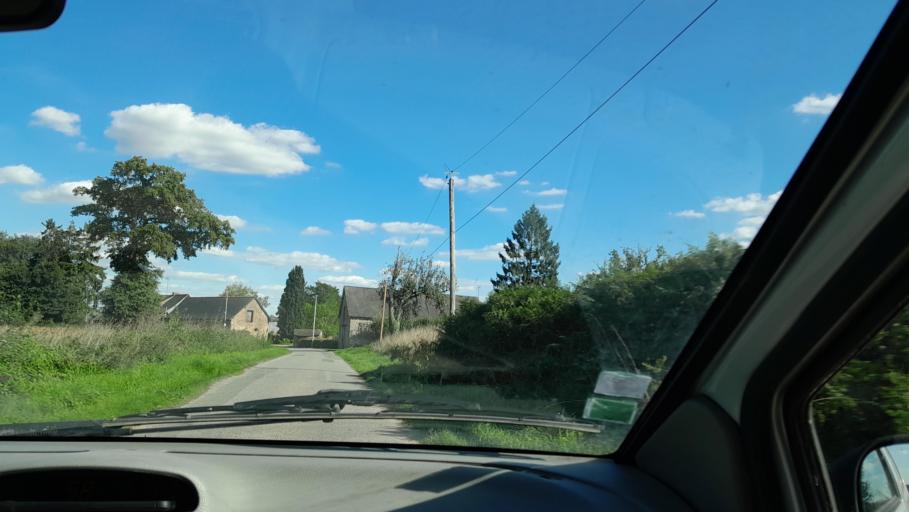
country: FR
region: Pays de la Loire
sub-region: Departement de la Mayenne
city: Ballots
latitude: 47.9543
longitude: -1.0733
